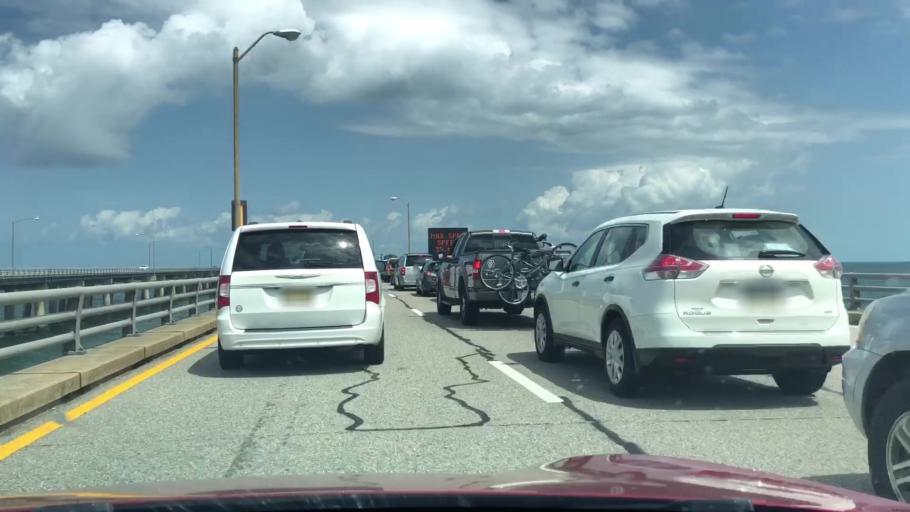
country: US
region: Virginia
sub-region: City of Virginia Beach
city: Virginia Beach
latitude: 36.9308
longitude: -76.1255
